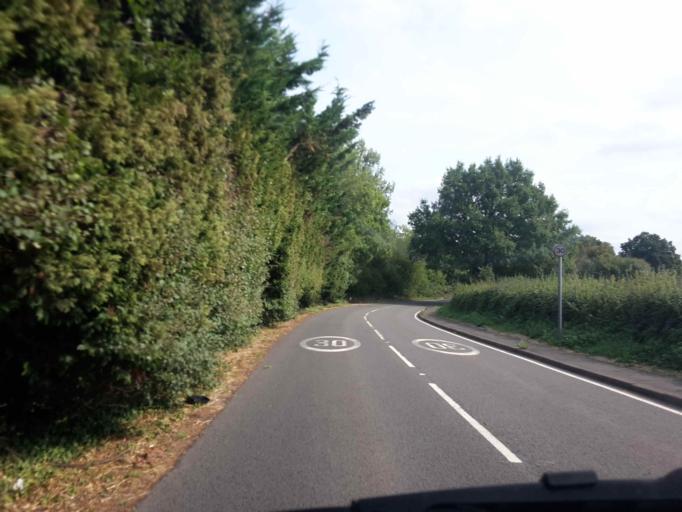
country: GB
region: England
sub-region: Wokingham
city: Twyford
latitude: 51.4532
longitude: -0.8496
